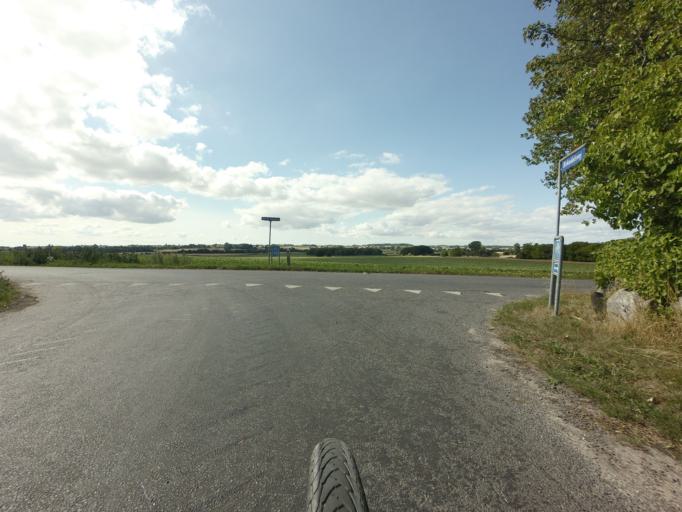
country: DK
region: Zealand
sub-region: Vordingborg Kommune
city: Stege
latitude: 55.0078
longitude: 12.4610
